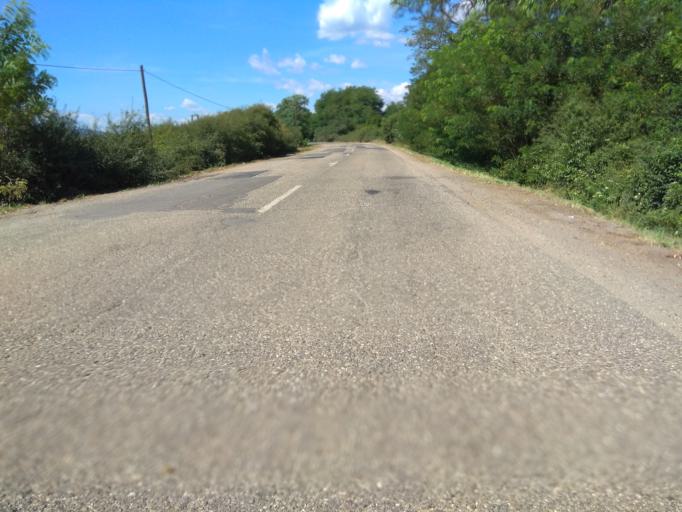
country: HU
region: Borsod-Abauj-Zemplen
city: Kazincbarcika
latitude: 48.2835
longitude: 20.6292
